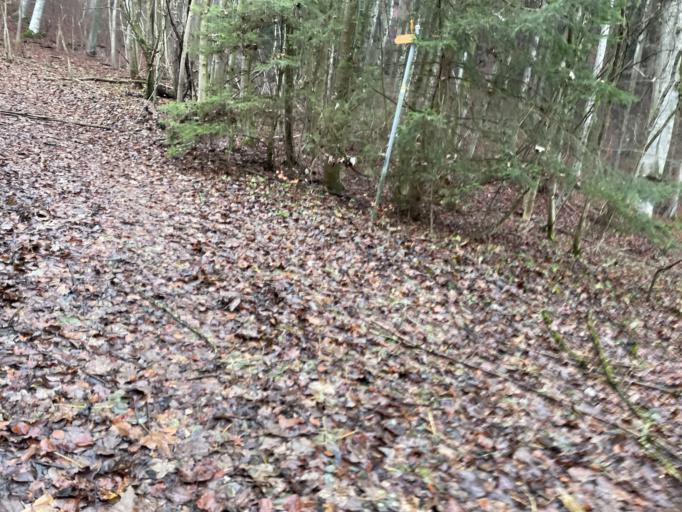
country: CH
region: Bern
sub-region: Bern-Mittelland District
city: Munsingen
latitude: 46.8732
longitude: 7.5352
